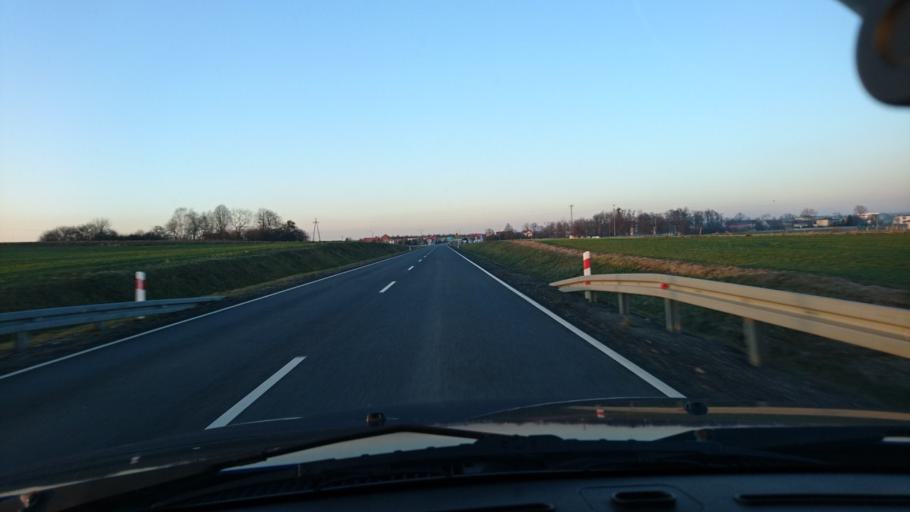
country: PL
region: Silesian Voivodeship
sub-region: Powiat gliwicki
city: Wielowies
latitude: 50.5002
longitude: 18.6057
